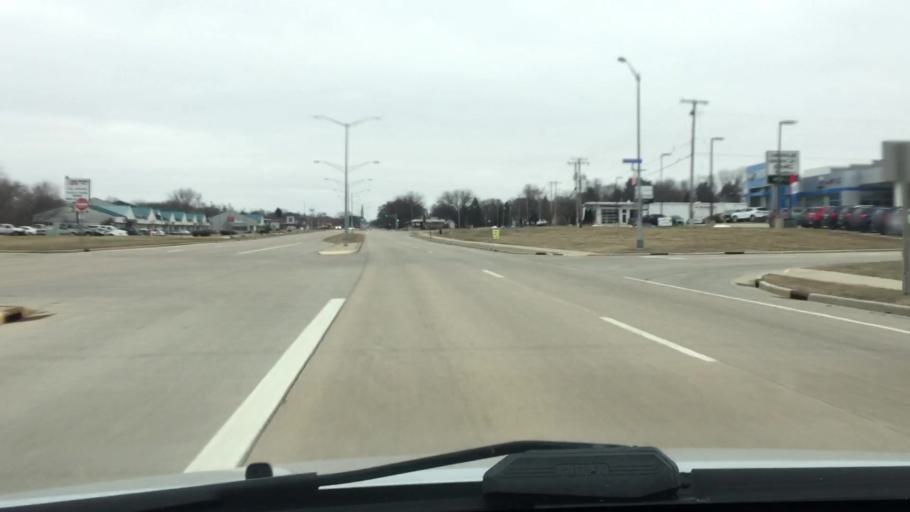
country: US
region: Wisconsin
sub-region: Jefferson County
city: Watertown
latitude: 43.1719
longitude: -88.7322
